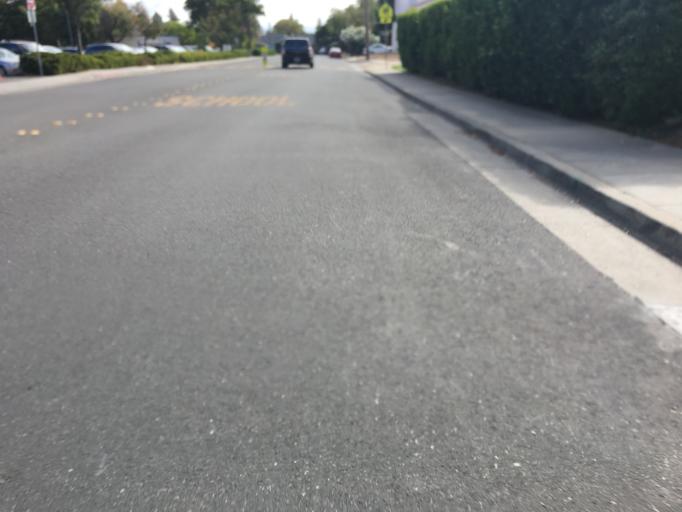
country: US
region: California
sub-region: Santa Clara County
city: Cupertino
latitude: 37.3303
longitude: -122.0461
